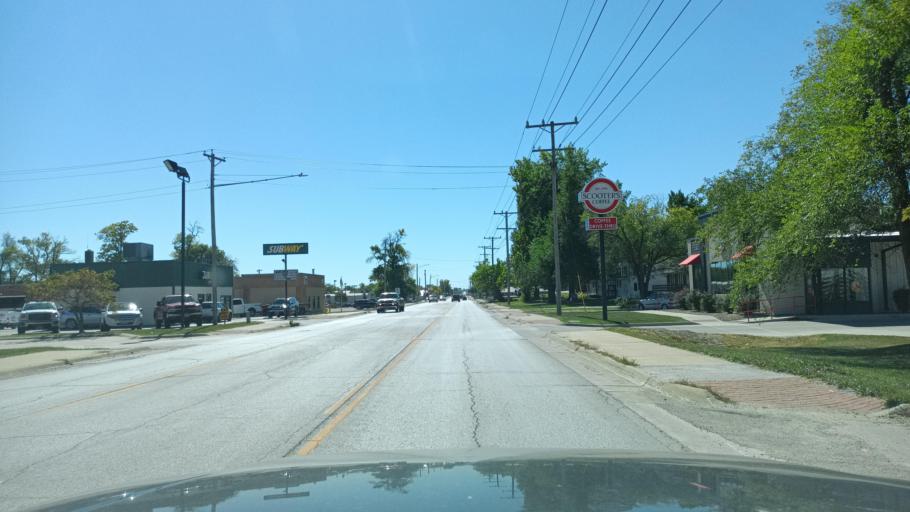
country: US
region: Missouri
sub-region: Adair County
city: Kirksville
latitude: 40.1840
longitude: -92.5720
